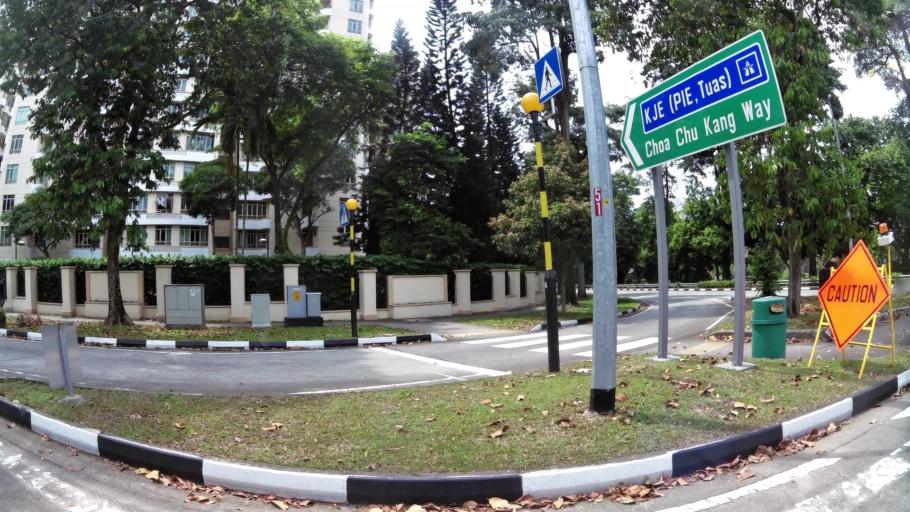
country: MY
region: Johor
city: Johor Bahru
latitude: 1.3887
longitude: 103.7457
